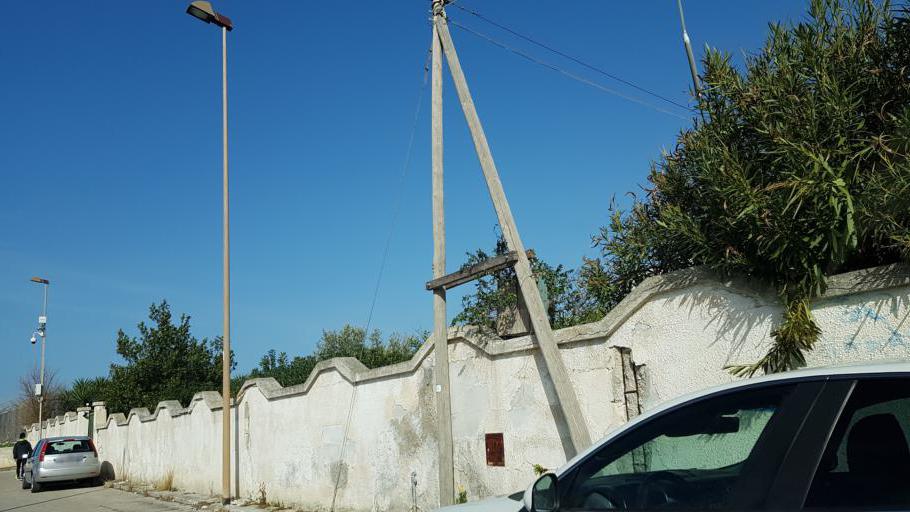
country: IT
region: Apulia
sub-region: Provincia di Brindisi
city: Brindisi
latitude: 40.6504
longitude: 17.9375
